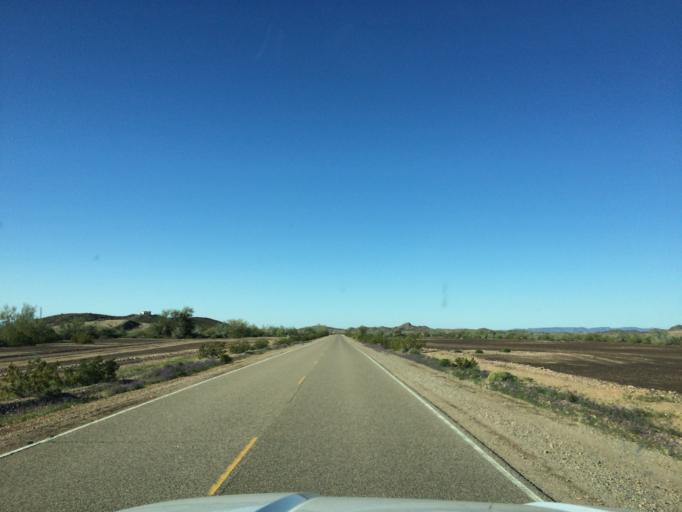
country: US
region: Arizona
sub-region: Yuma County
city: Wellton
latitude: 32.9704
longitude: -114.2831
